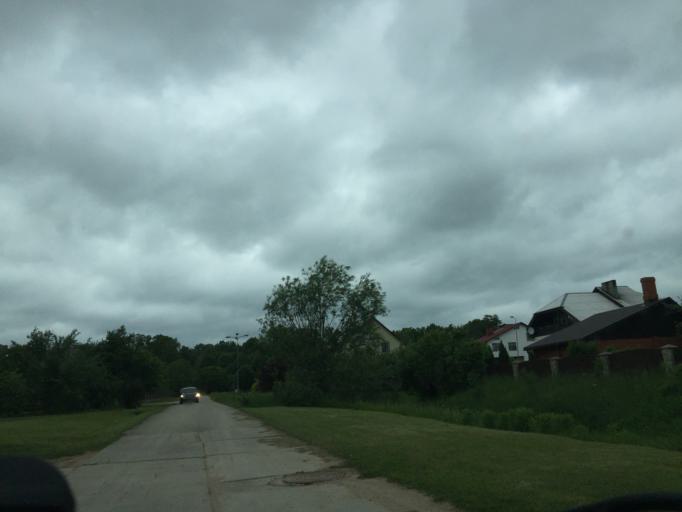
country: LV
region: Valmieras Rajons
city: Valmiera
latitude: 57.5534
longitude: 25.4201
